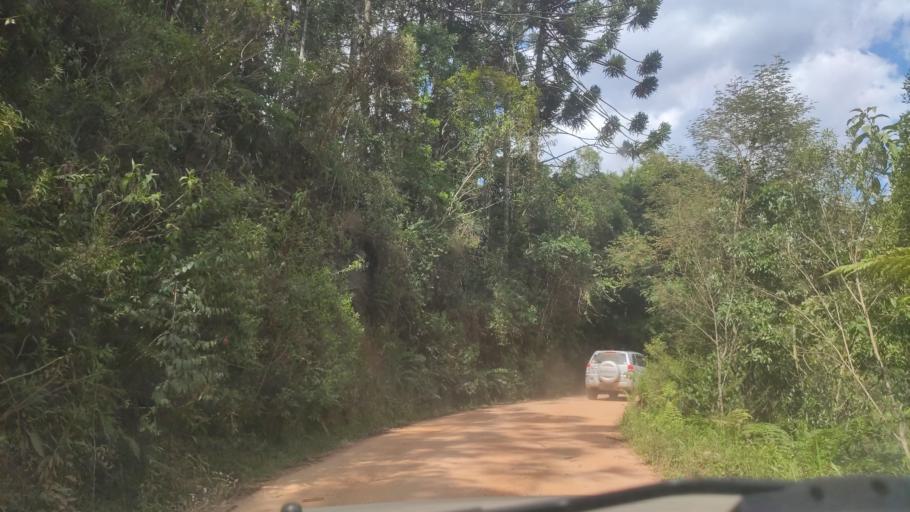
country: BR
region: Minas Gerais
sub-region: Camanducaia
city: Camanducaia
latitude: -22.7685
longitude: -45.9937
